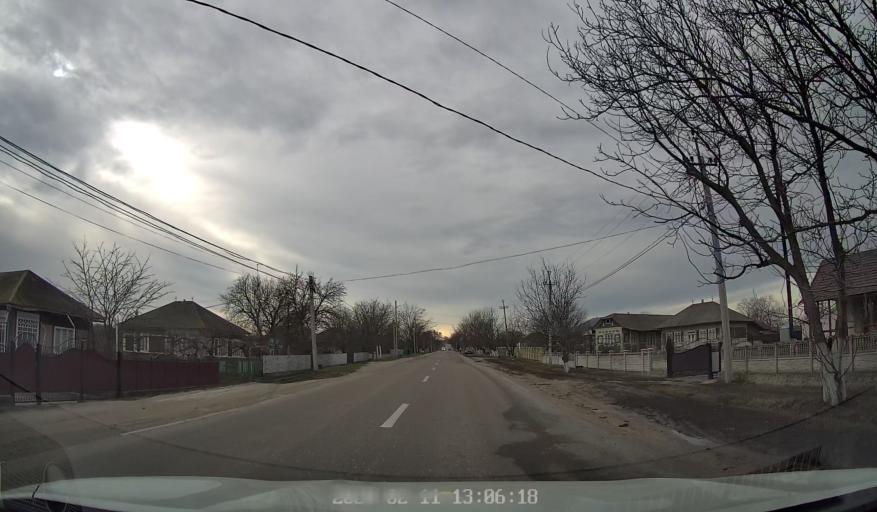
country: RO
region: Botosani
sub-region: Comuna Radauti-Prut
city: Miorcani
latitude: 48.2925
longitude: 26.9240
